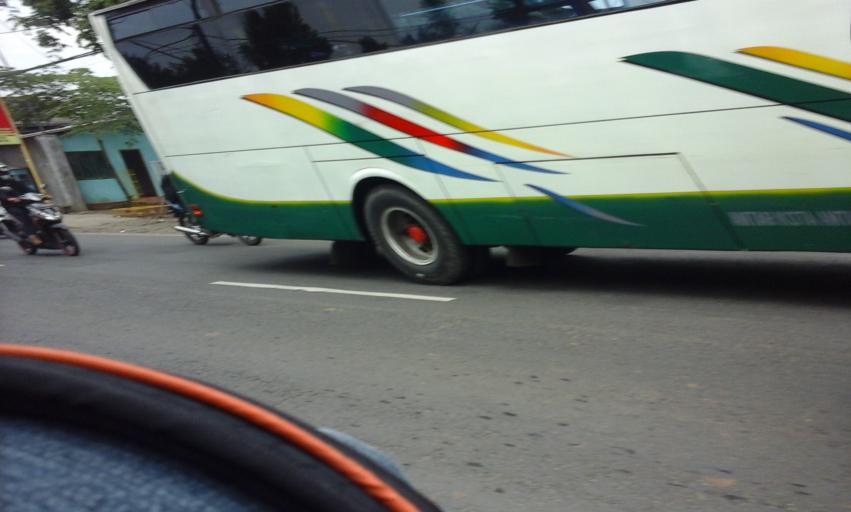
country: ID
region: East Java
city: Jubung
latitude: -8.1982
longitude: 113.6305
